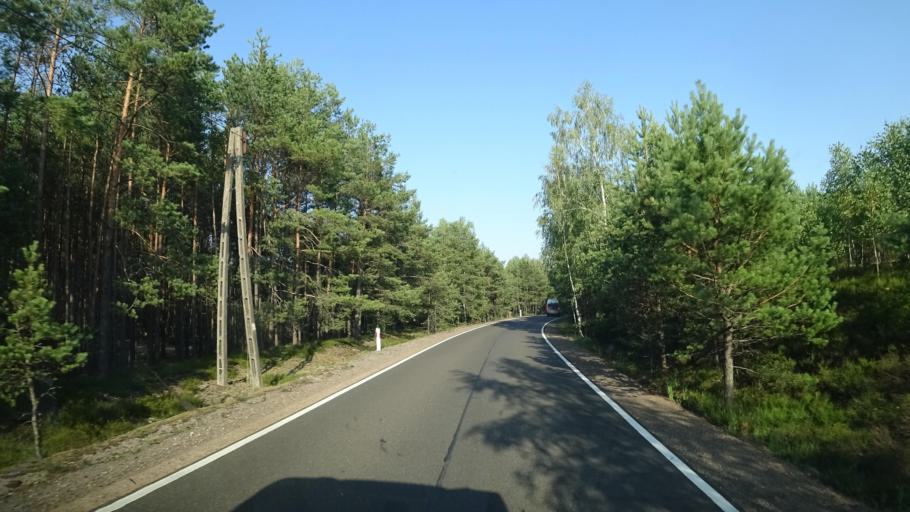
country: PL
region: Pomeranian Voivodeship
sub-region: Powiat chojnicki
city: Chojnice
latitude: 53.8558
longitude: 17.5535
